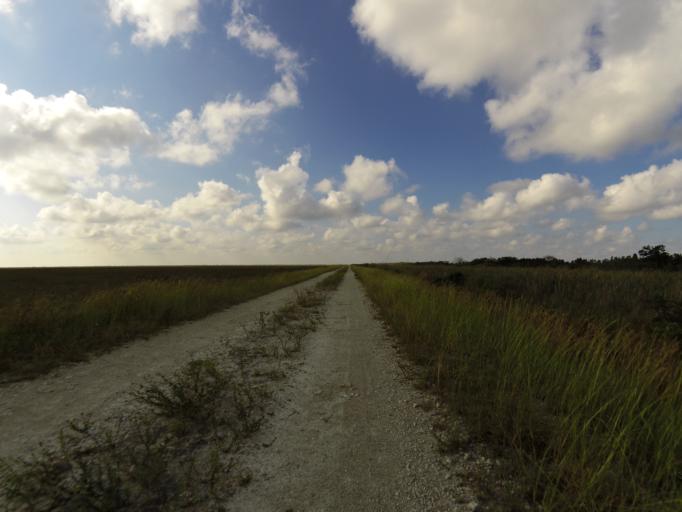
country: US
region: Florida
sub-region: Broward County
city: Weston
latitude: 26.0422
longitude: -80.4867
